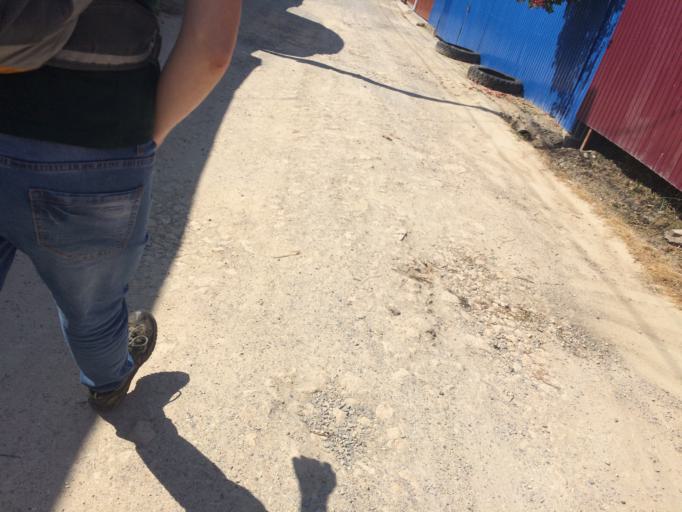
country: RU
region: Stavropol'skiy
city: Tatarka
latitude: 44.9857
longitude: 41.9420
